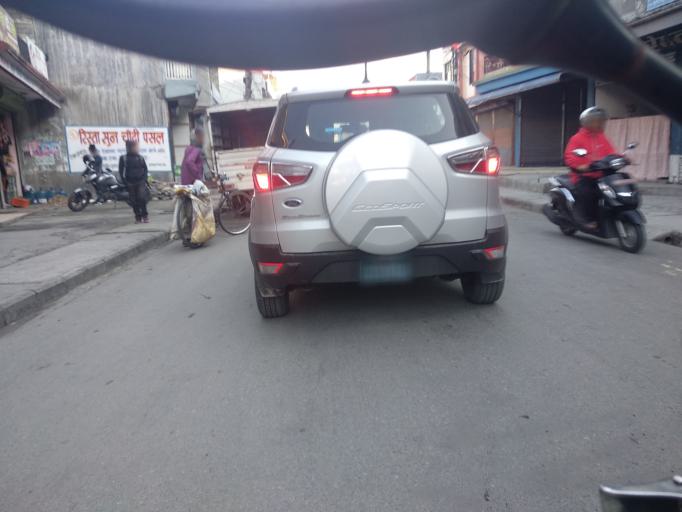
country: NP
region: Western Region
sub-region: Gandaki Zone
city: Pokhara
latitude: 28.2410
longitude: 83.9882
